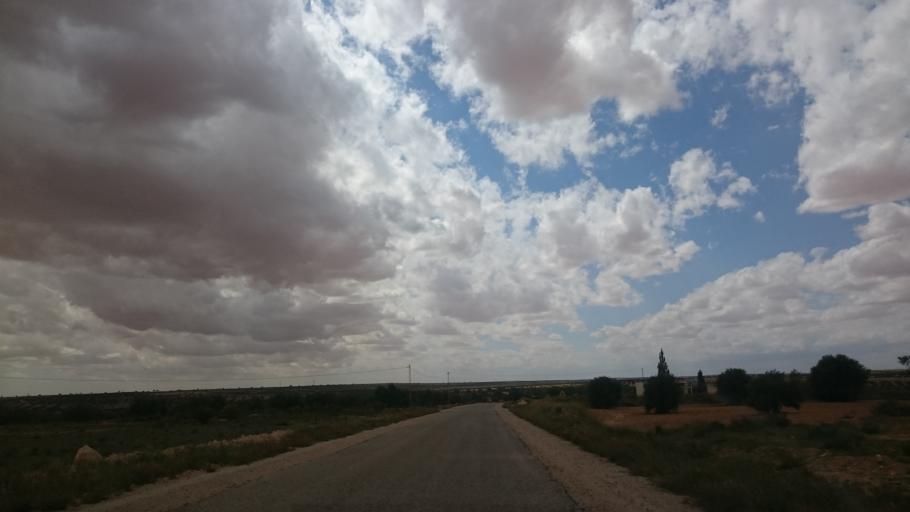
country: TN
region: Safaqis
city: Bi'r `Ali Bin Khalifah
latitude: 34.7787
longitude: 10.3734
